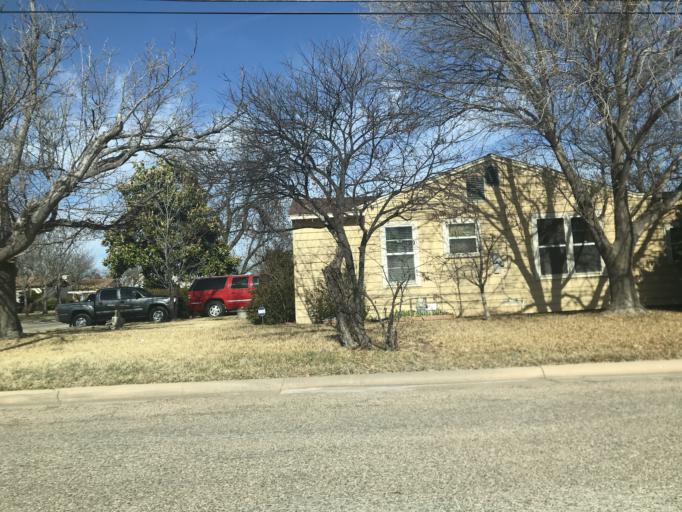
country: US
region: Texas
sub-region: Taylor County
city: Abilene
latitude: 32.4211
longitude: -99.7514
